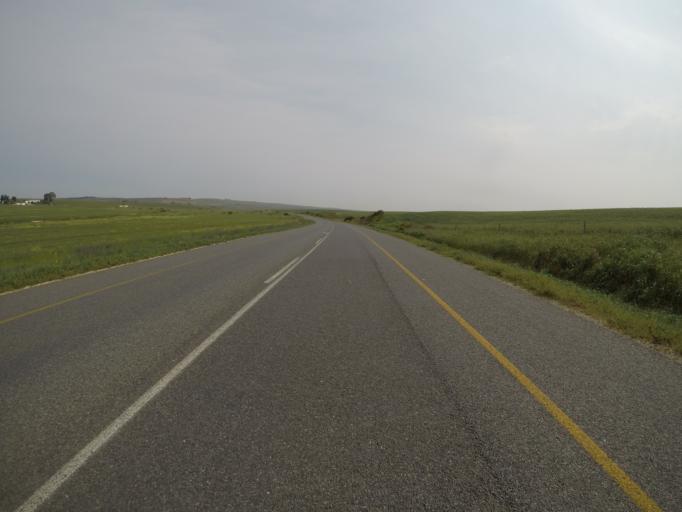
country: ZA
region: Western Cape
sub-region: West Coast District Municipality
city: Malmesbury
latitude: -33.4546
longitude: 18.7811
